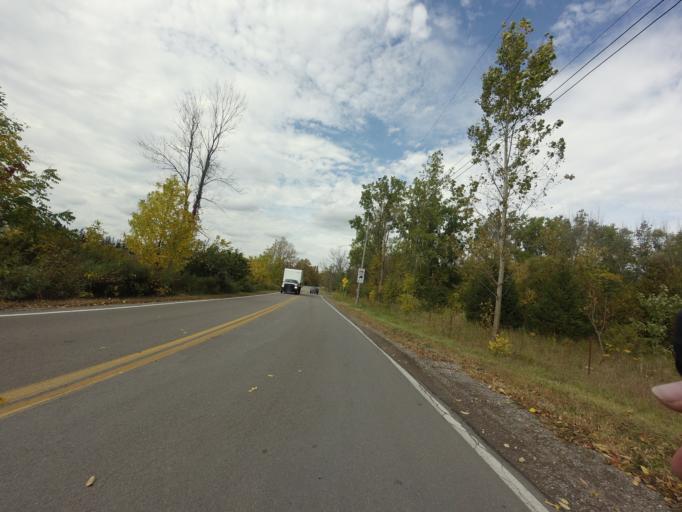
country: CA
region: Ontario
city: Burlington
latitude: 43.3576
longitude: -79.8770
